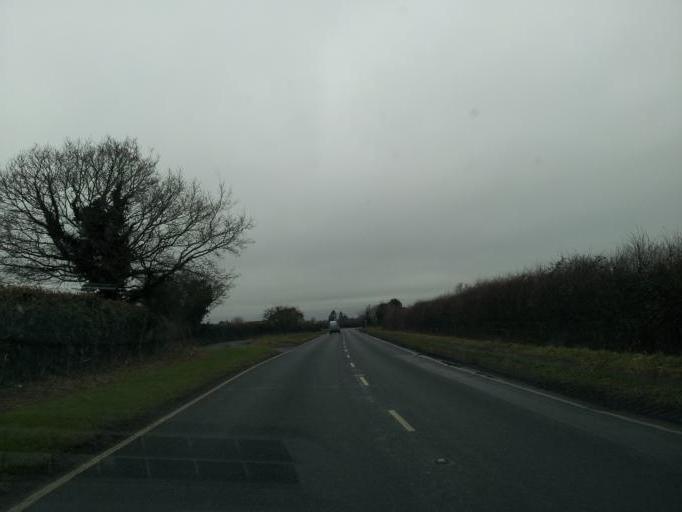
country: GB
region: England
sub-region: Essex
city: Mistley
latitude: 51.9680
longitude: 1.0801
